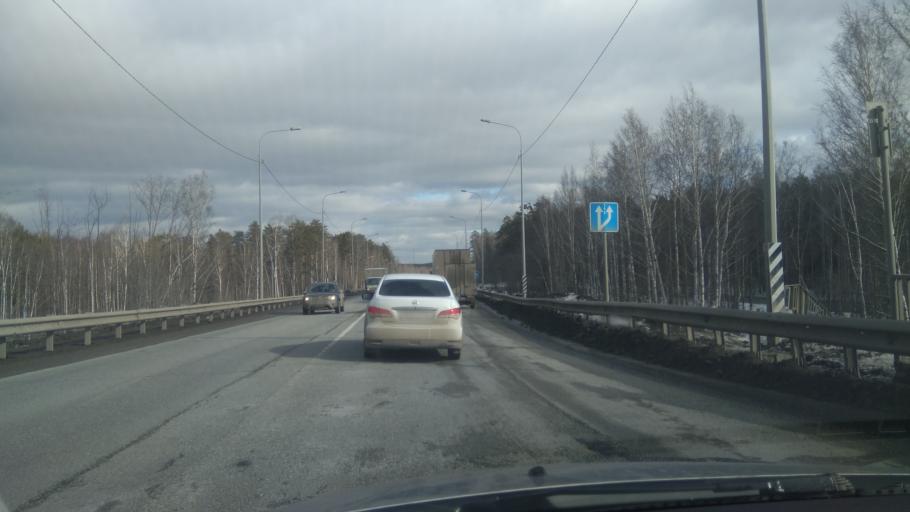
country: RU
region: Sverdlovsk
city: Talitsa
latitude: 56.8495
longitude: 60.0612
